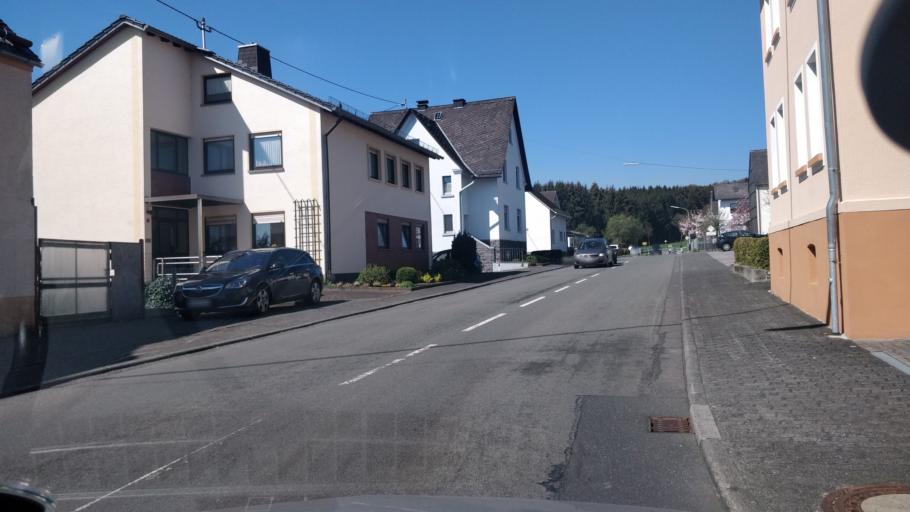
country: DE
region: Rheinland-Pfalz
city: Winnen
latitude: 50.5719
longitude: 8.0089
